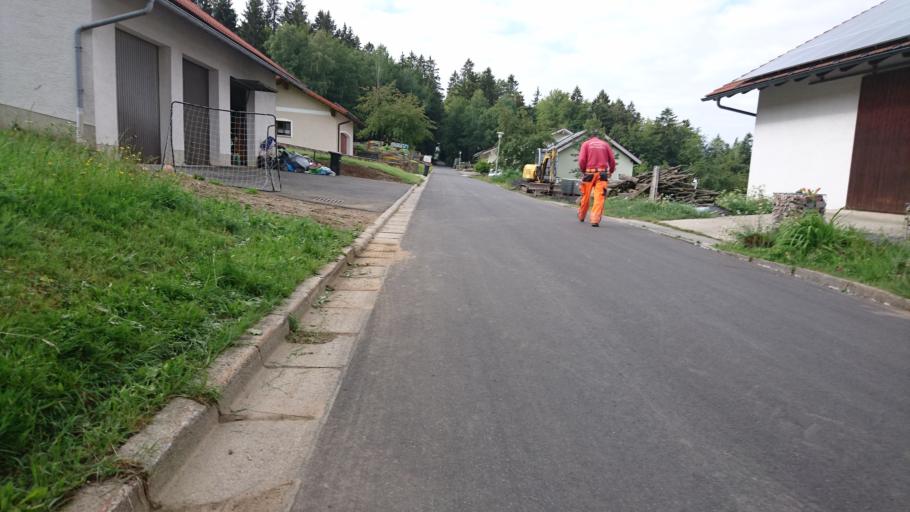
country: DE
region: Bavaria
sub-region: Lower Bavaria
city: Neuschonau
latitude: 48.8796
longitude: 13.4788
